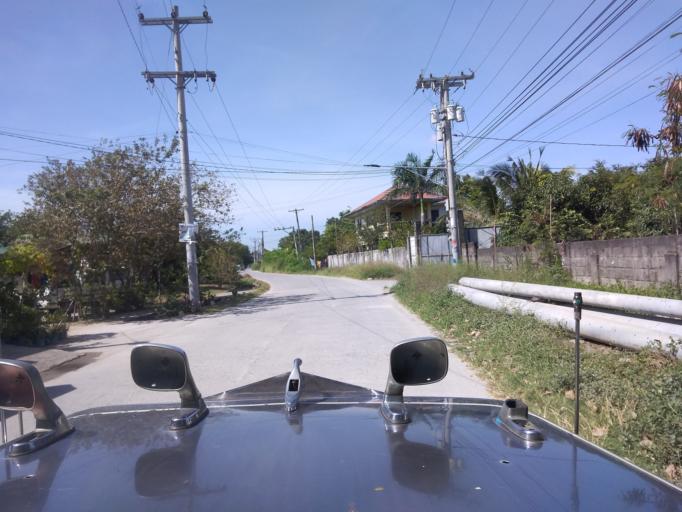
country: PH
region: Central Luzon
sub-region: Province of Pampanga
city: Magliman
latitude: 15.0183
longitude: 120.6584
